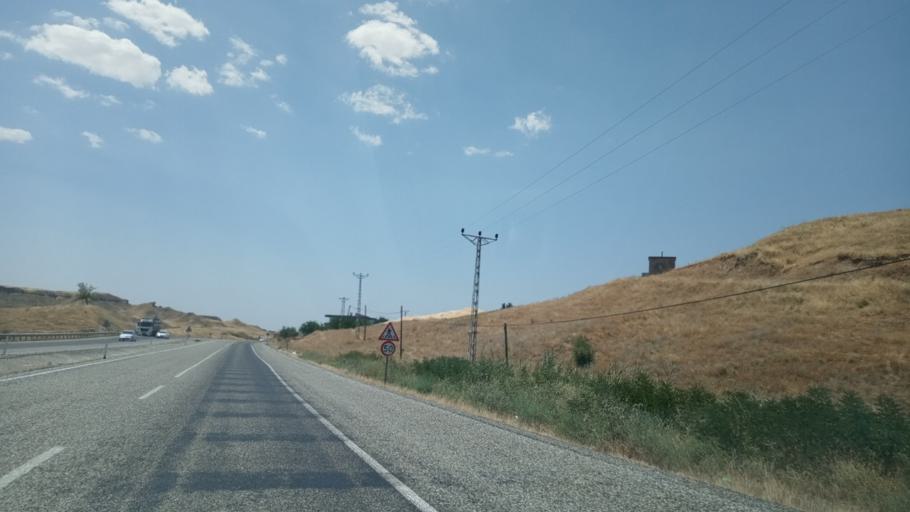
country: TR
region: Batman
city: Bekirhan
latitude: 38.1538
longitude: 41.3202
